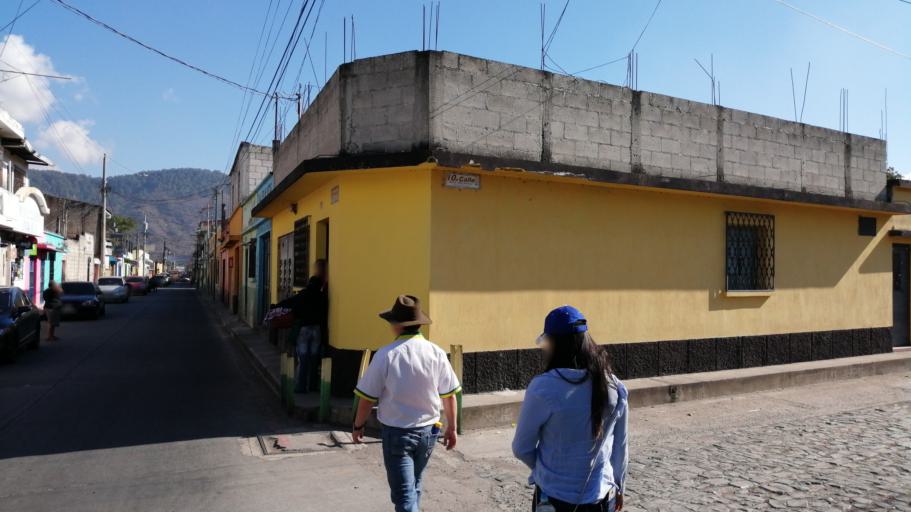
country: GT
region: Guatemala
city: Amatitlan
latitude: 14.4764
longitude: -90.6209
